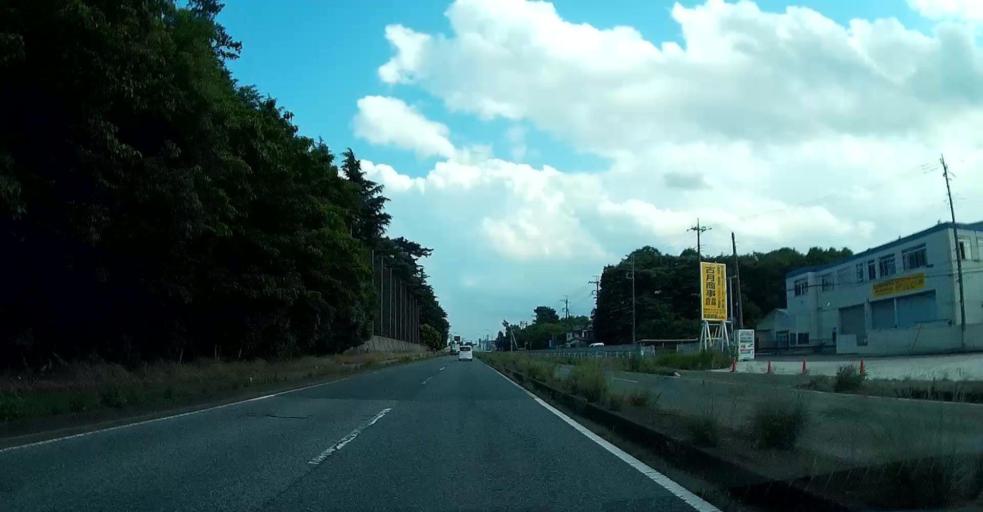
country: JP
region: Chiba
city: Noda
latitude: 35.9662
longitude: 139.8682
